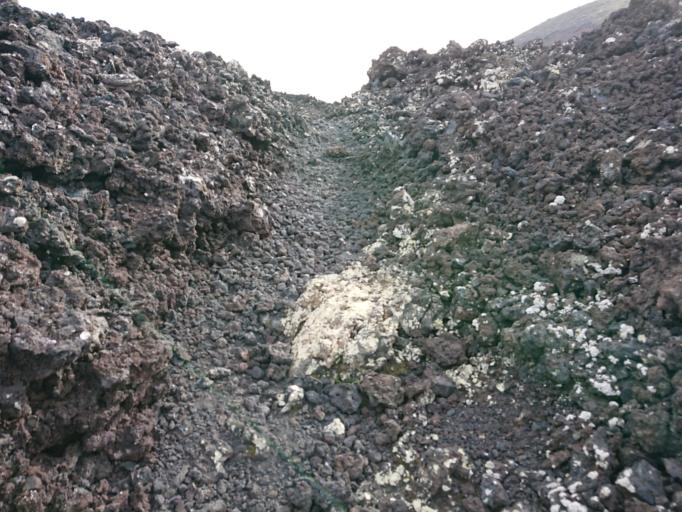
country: ES
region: Canary Islands
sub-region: Provincia de Las Palmas
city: Tinajo
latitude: 29.0117
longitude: -13.6774
